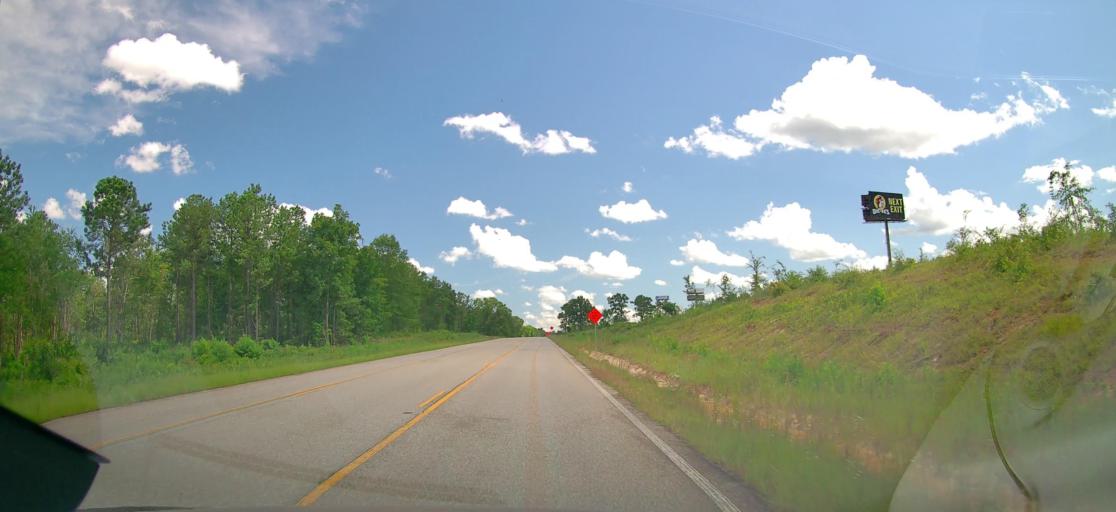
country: US
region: Georgia
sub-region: Peach County
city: Byron
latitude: 32.6078
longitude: -83.7407
